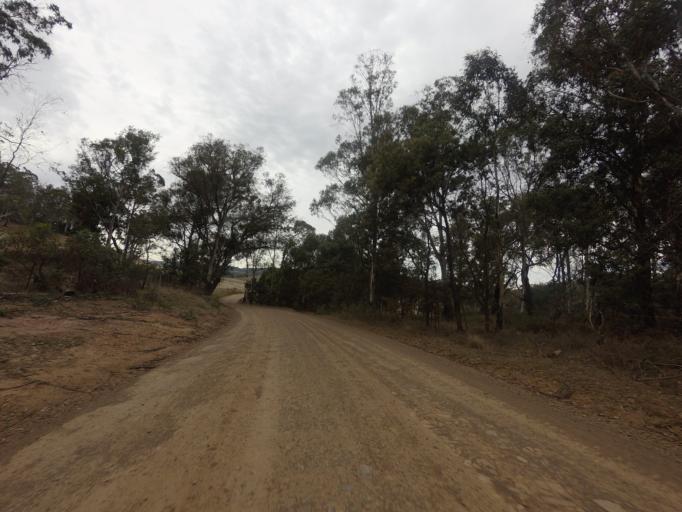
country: AU
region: Tasmania
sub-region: Derwent Valley
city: New Norfolk
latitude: -42.5617
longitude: 146.9451
